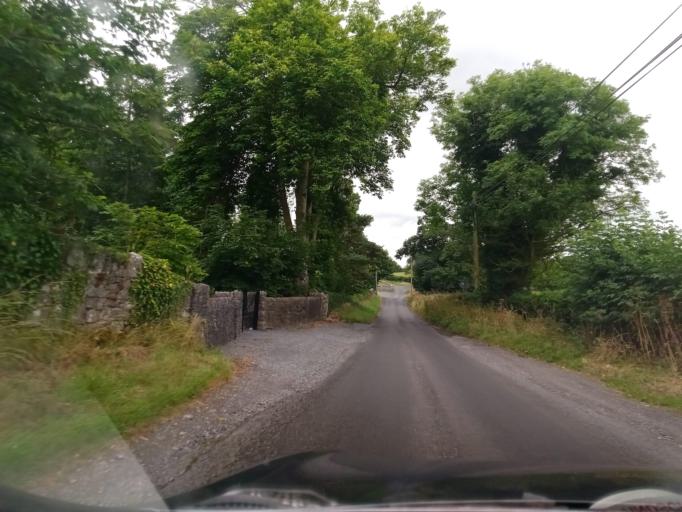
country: IE
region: Leinster
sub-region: Laois
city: Stradbally
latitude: 52.9921
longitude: -7.1764
